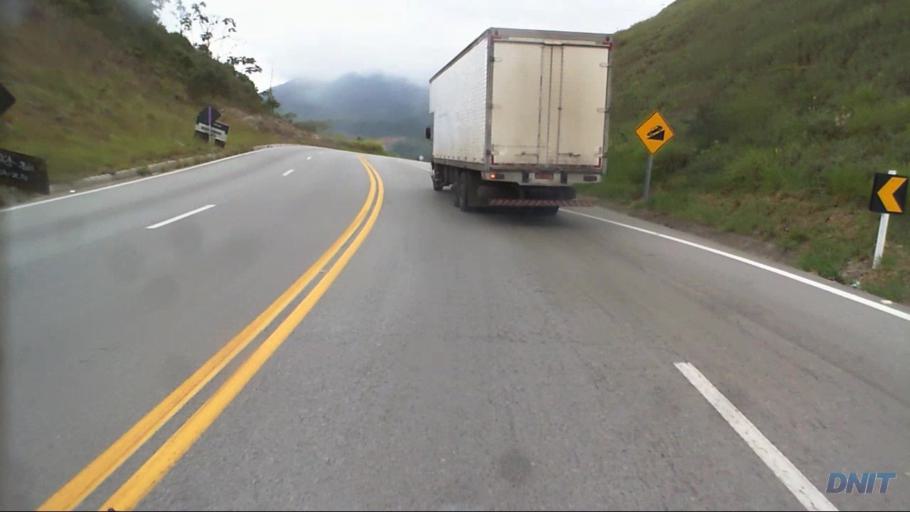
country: BR
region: Minas Gerais
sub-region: Nova Era
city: Nova Era
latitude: -19.6514
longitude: -42.9466
